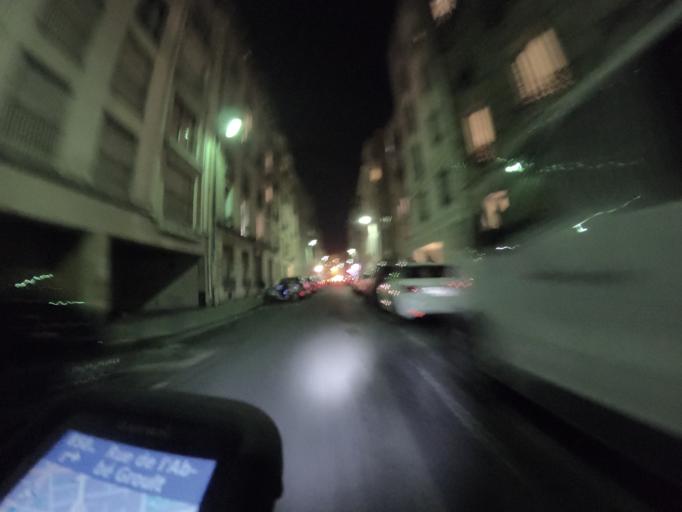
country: FR
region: Ile-de-France
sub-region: Departement des Hauts-de-Seine
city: Vanves
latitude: 48.8413
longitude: 2.2950
